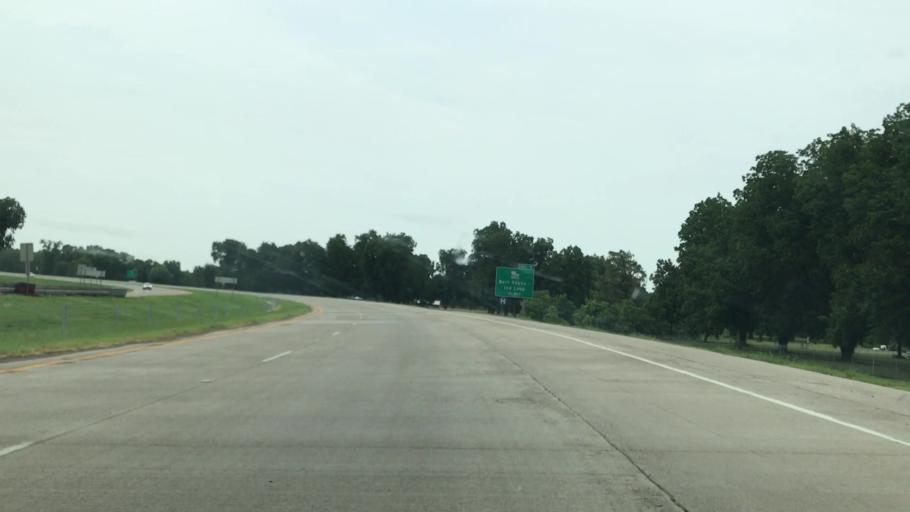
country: US
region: Louisiana
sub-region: Bossier Parish
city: Bossier City
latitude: 32.4045
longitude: -93.7144
